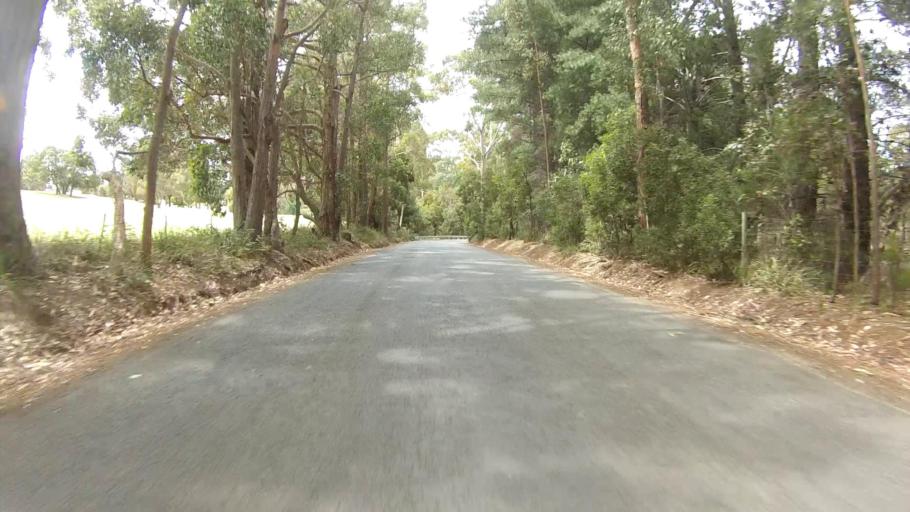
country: AU
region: Tasmania
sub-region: Kingborough
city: Margate
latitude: -43.0087
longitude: 147.2834
